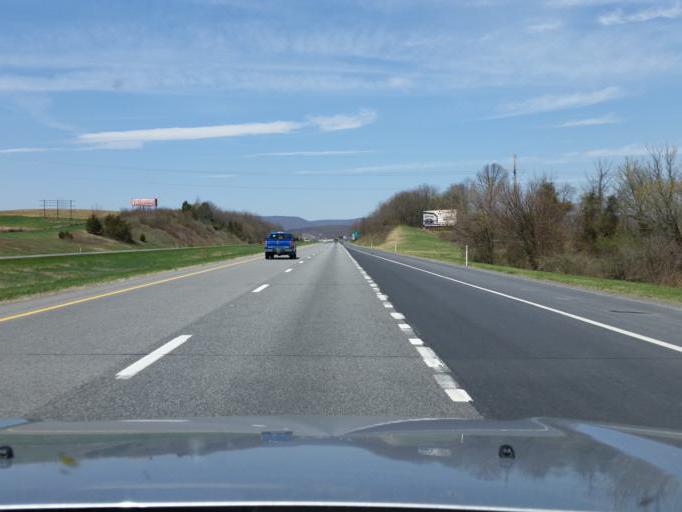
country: US
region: Pennsylvania
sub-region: Juniata County
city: Mifflintown
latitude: 40.5605
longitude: -77.3637
